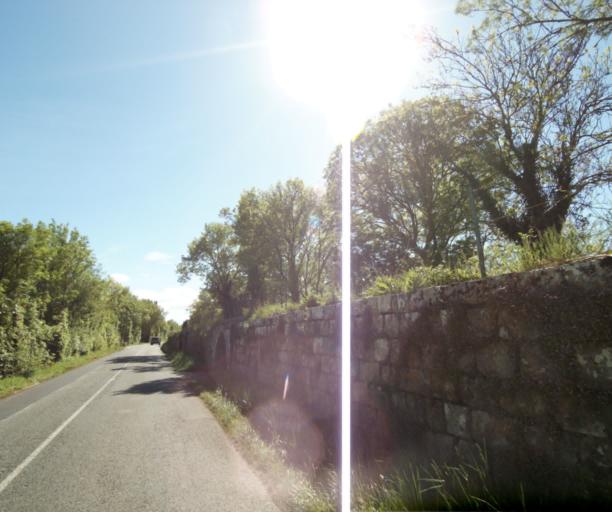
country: FR
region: Poitou-Charentes
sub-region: Departement de la Charente-Maritime
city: Bussac-sur-Charente
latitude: 45.8302
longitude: -0.6519
